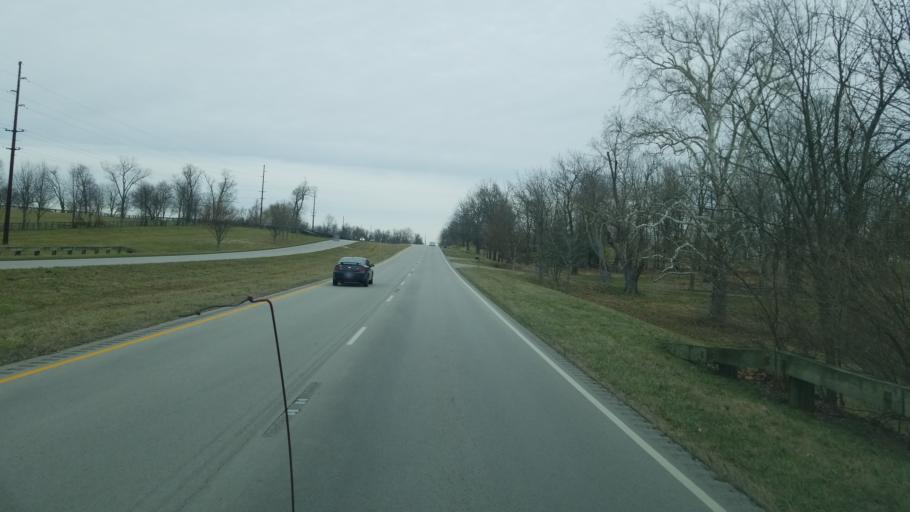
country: US
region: Kentucky
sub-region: Bourbon County
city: Paris
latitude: 38.1583
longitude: -84.3302
